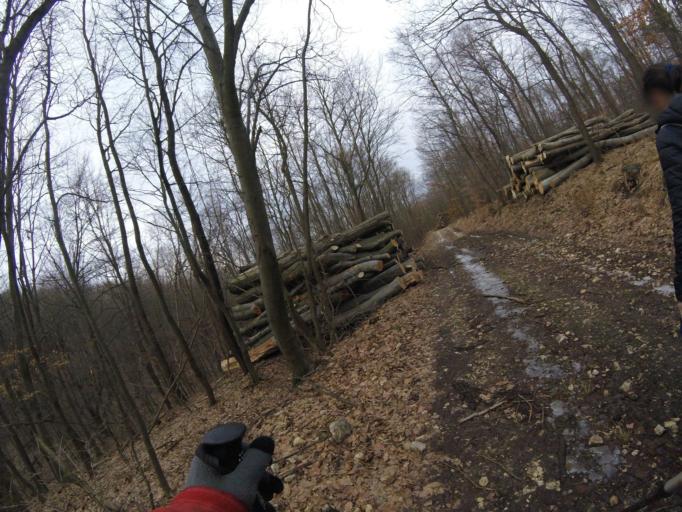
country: HU
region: Komarom-Esztergom
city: Kesztolc
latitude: 47.7218
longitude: 18.8228
